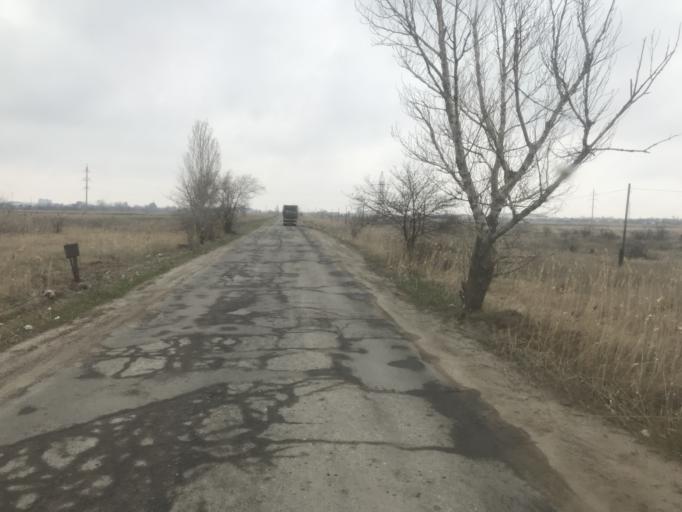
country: RU
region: Volgograd
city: Svetlyy Yar
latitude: 48.5167
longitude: 44.6298
